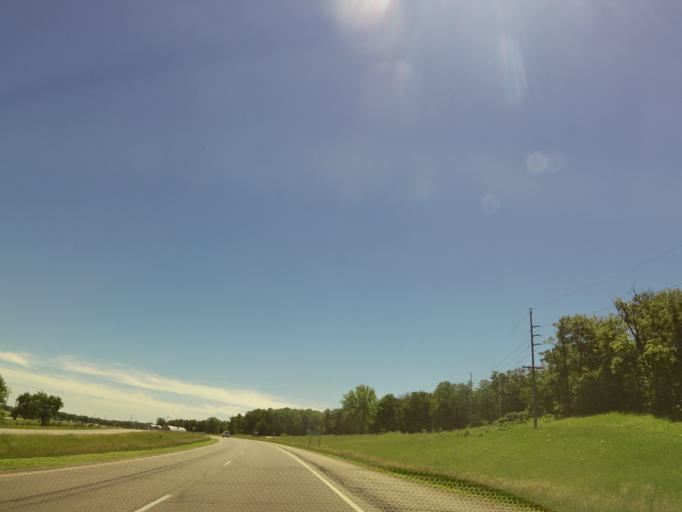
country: US
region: Minnesota
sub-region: Becker County
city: Frazee
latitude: 46.7430
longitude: -95.7601
